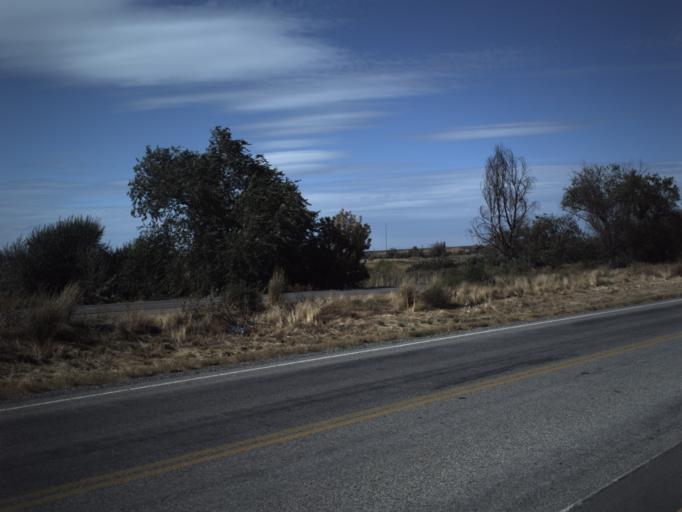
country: US
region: Utah
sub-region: Davis County
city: North Salt Lake
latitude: 40.8244
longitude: -111.9375
